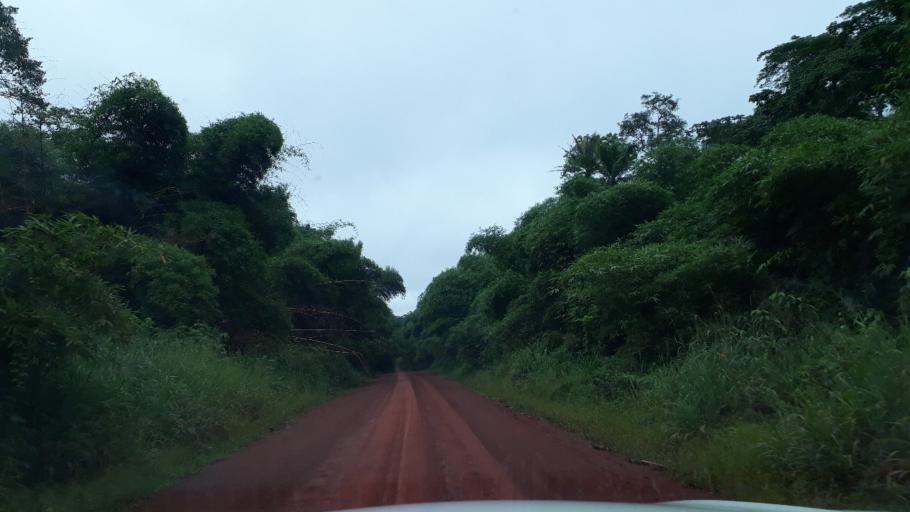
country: CD
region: Eastern Province
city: Wamba
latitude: 1.3508
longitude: 27.5897
